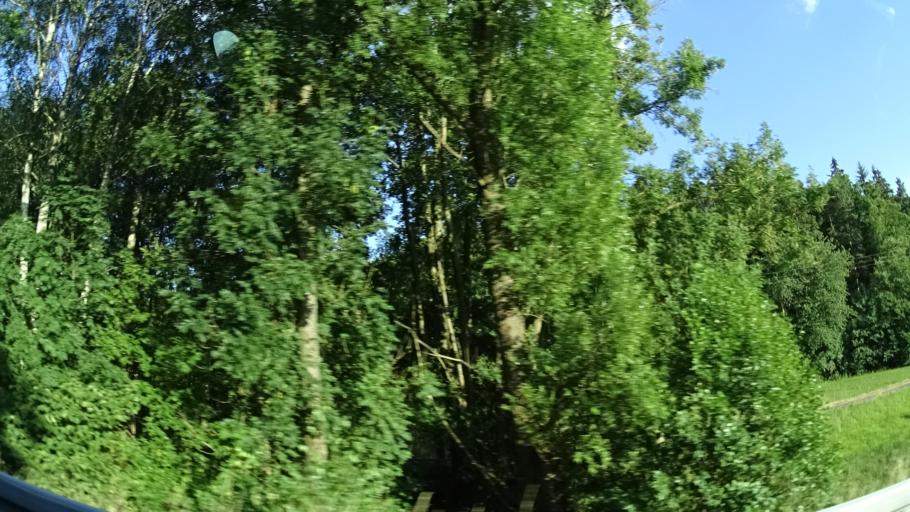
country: DE
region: Bavaria
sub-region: Regierungsbezirk Unterfranken
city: Oberelsbach
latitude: 50.4230
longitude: 10.1215
